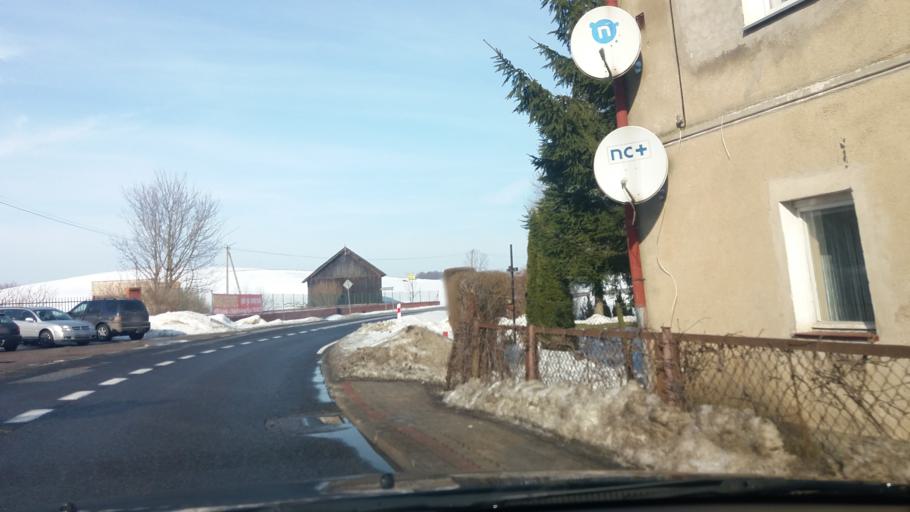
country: PL
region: Warmian-Masurian Voivodeship
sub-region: Powiat olsztynski
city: Czerwonka
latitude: 53.9358
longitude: 20.8834
